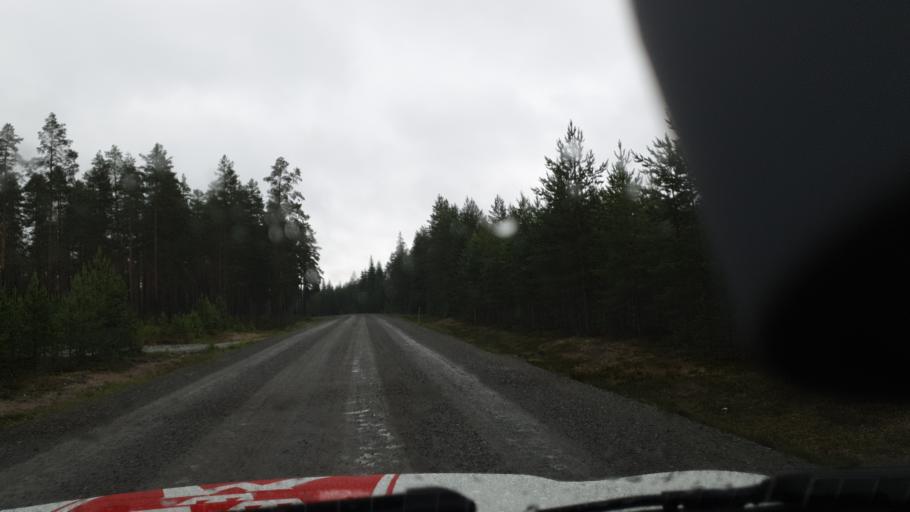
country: SE
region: Vaesterbotten
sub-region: Nordmalings Kommun
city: Nordmaling
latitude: 63.7063
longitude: 19.6286
